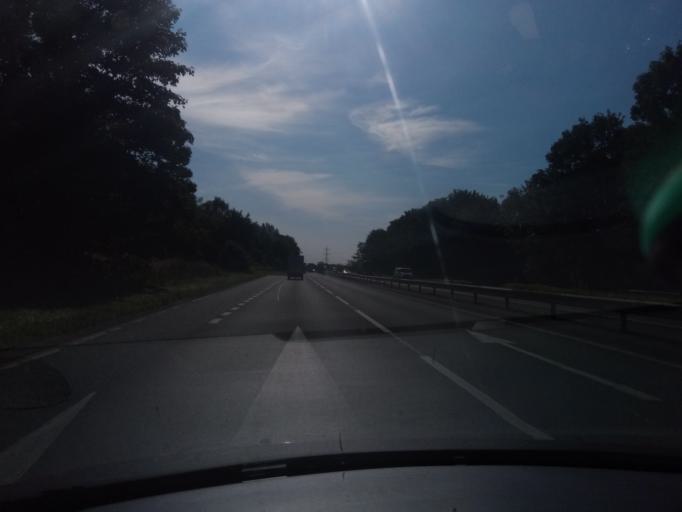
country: GB
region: England
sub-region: North Yorkshire
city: Thirsk
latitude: 54.2818
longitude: -1.3408
